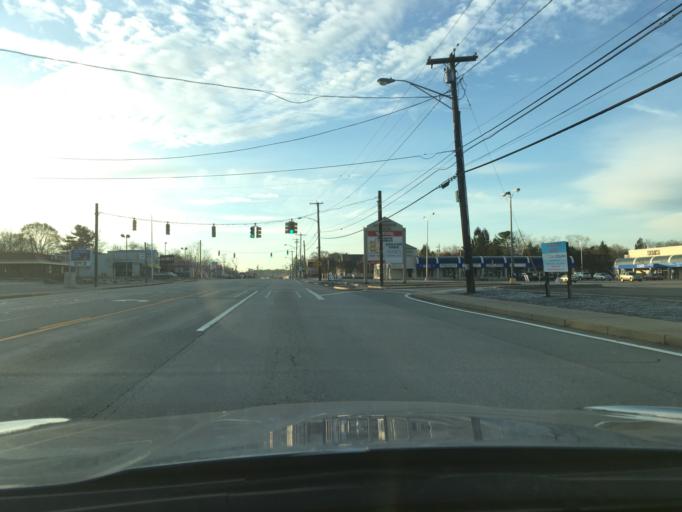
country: US
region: Rhode Island
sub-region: Kent County
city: East Greenwich
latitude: 41.6176
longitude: -71.4581
